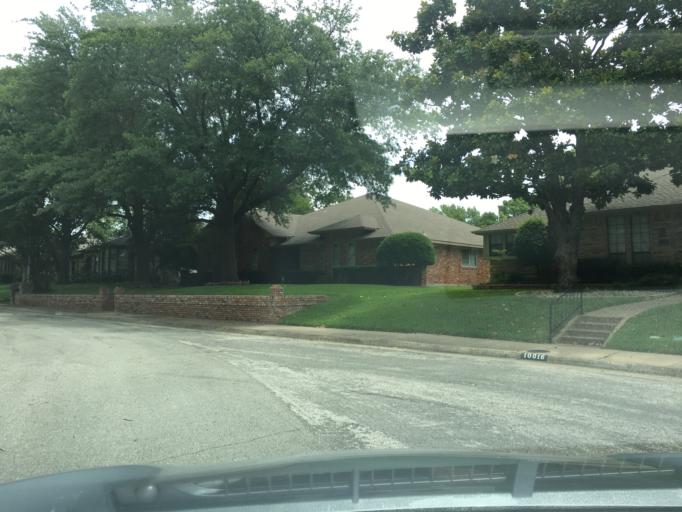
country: US
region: Texas
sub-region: Dallas County
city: Richardson
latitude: 32.9157
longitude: -96.7135
